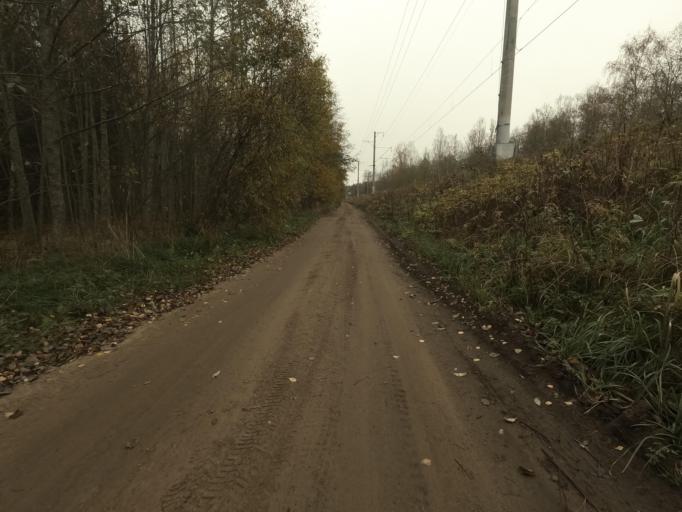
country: RU
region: Leningrad
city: Pavlovo
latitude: 59.7838
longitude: 30.8943
